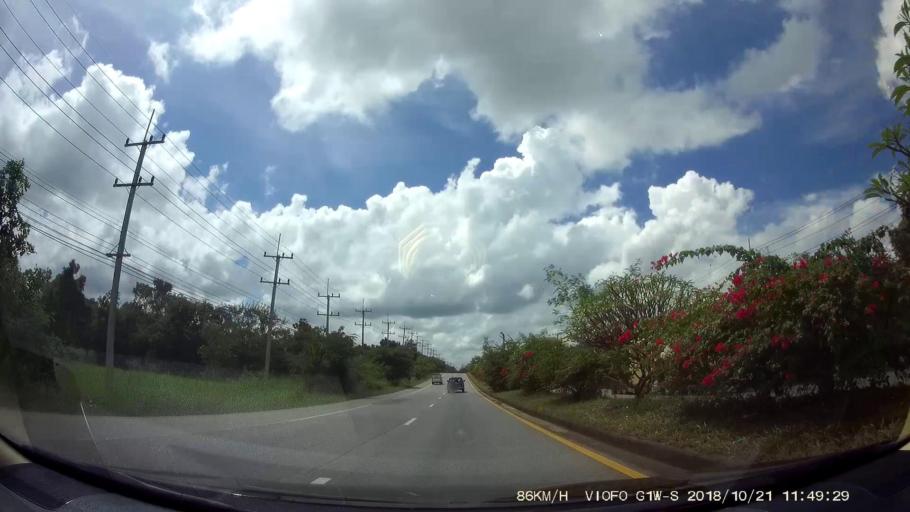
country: TH
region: Chaiyaphum
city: Noen Sa-nga
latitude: 15.6387
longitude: 101.9408
